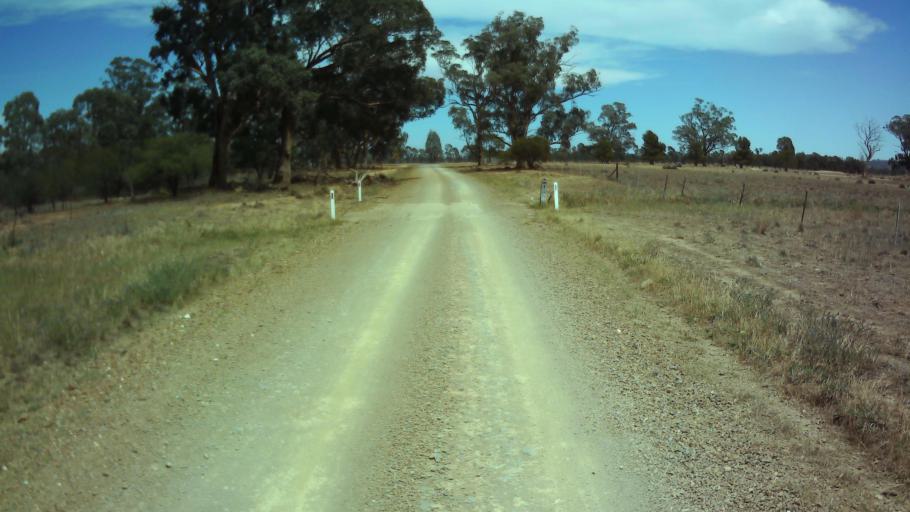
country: AU
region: New South Wales
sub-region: Weddin
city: Grenfell
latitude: -33.8562
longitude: 147.9058
